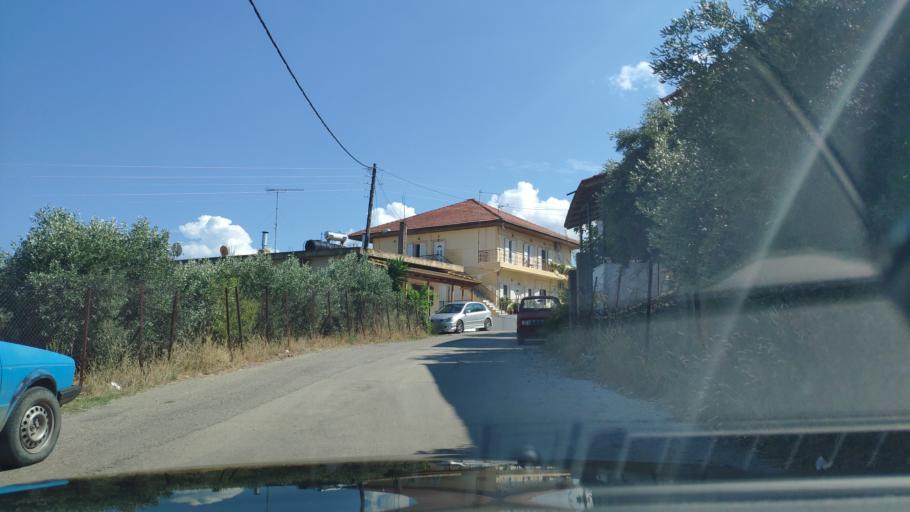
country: GR
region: West Greece
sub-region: Nomos Aitolias kai Akarnanias
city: Katouna
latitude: 38.7905
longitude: 21.1156
